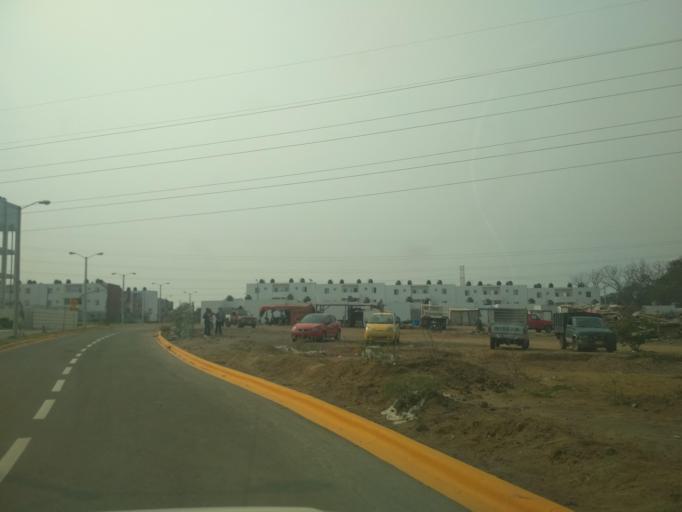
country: MX
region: Veracruz
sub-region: Veracruz
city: Las Amapolas
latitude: 19.1508
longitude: -96.2316
